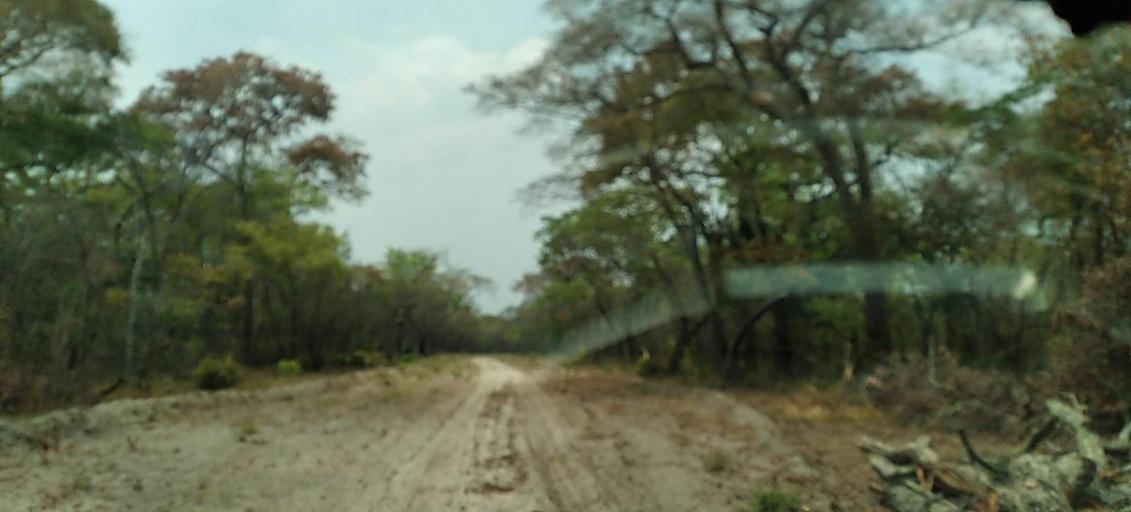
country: ZM
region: Western
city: Lukulu
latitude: -14.0072
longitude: 23.5835
